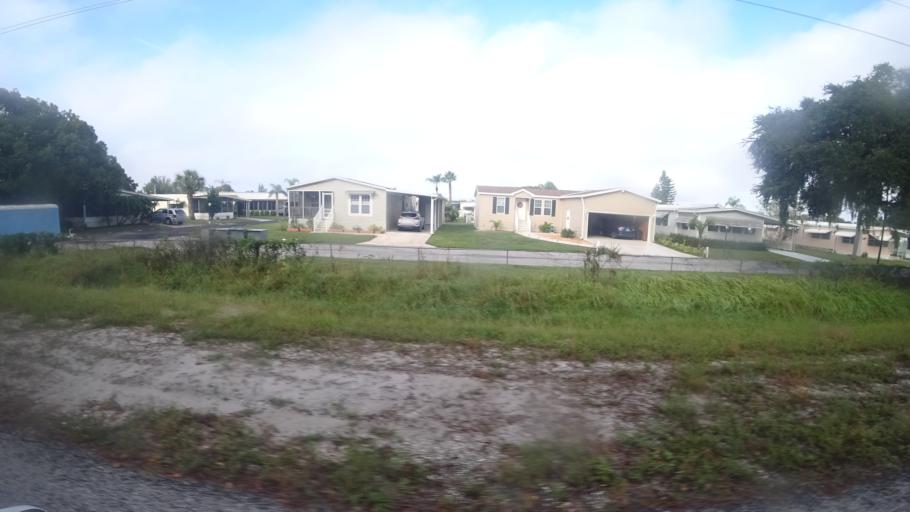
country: US
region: Florida
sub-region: Manatee County
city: Ellenton
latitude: 27.5325
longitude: -82.4827
